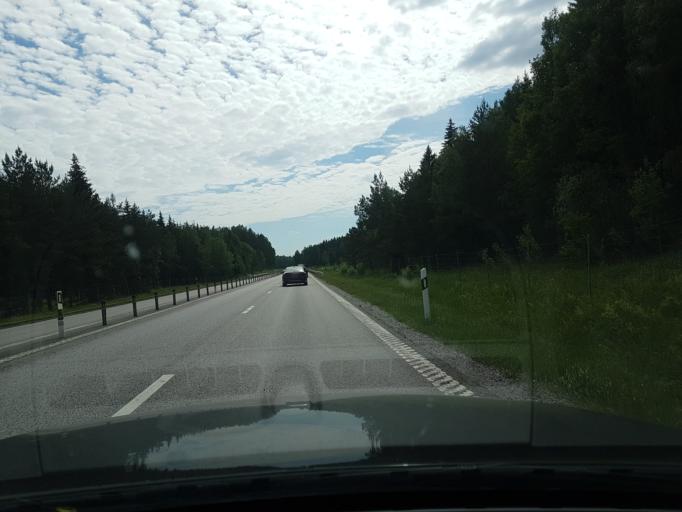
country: SE
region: Stockholm
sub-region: Vallentuna Kommun
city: Vallentuna
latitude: 59.5241
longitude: 18.1864
